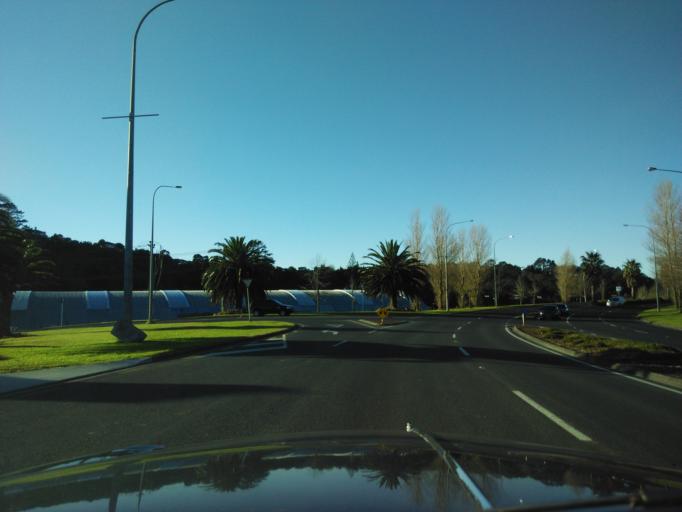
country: NZ
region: Auckland
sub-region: Auckland
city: Rothesay Bay
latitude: -36.7257
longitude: 174.6986
